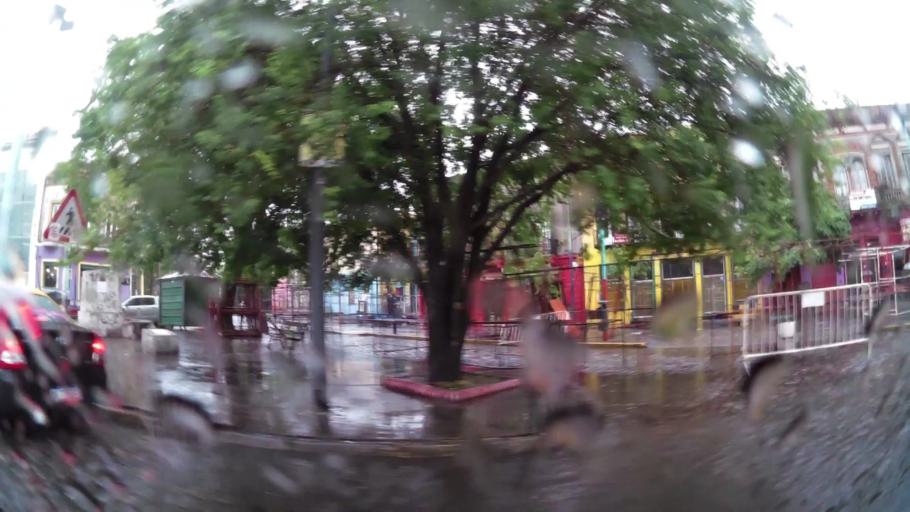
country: AR
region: Buenos Aires
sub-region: Partido de Avellaneda
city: Avellaneda
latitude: -34.6393
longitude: -58.3615
